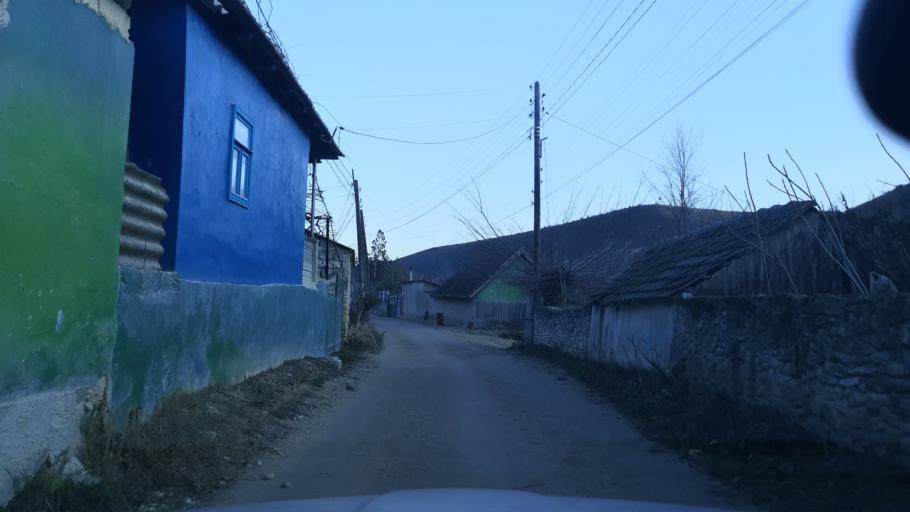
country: MD
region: Telenesti
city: Cocieri
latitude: 47.3010
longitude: 28.9688
